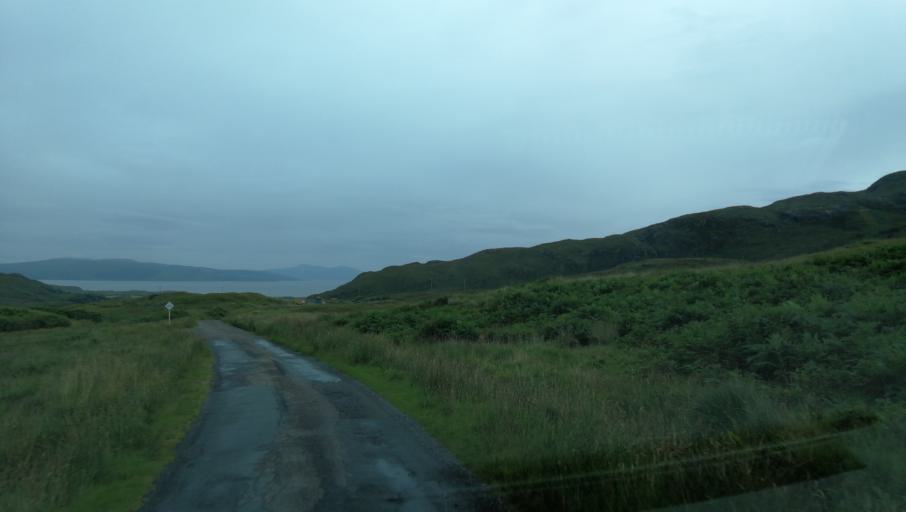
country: GB
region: Scotland
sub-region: Argyll and Bute
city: Isle Of Mull
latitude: 56.7104
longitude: -6.1403
